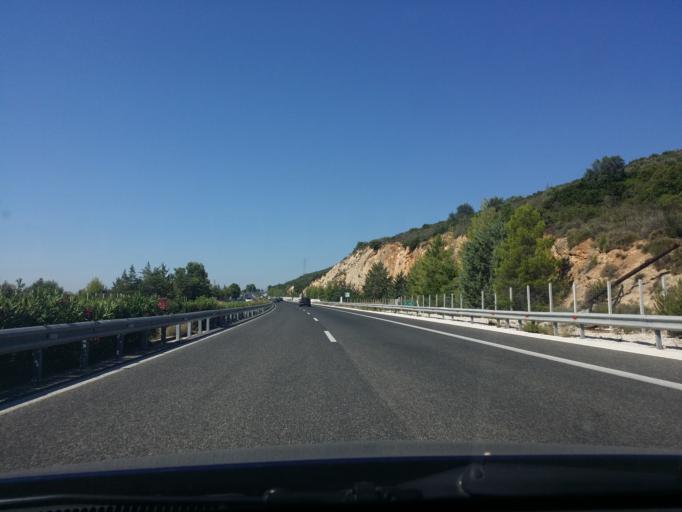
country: GR
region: Peloponnese
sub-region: Nomos Korinthias
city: Nemea
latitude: 37.7960
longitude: 22.7166
